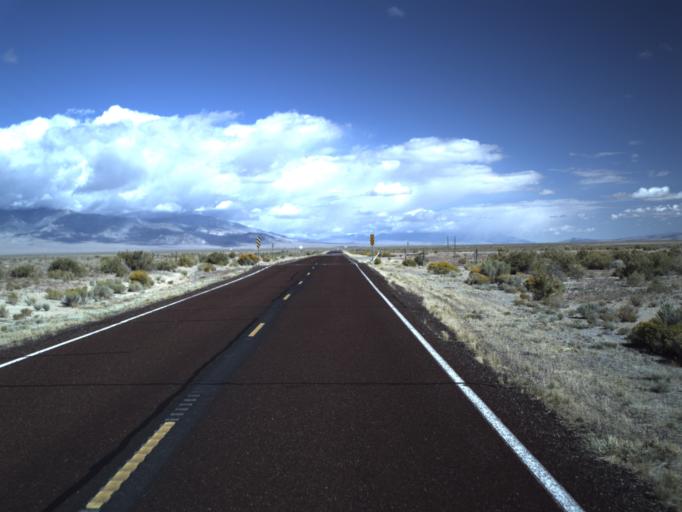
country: US
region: Nevada
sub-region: White Pine County
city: McGill
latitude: 38.9528
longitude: -114.0333
